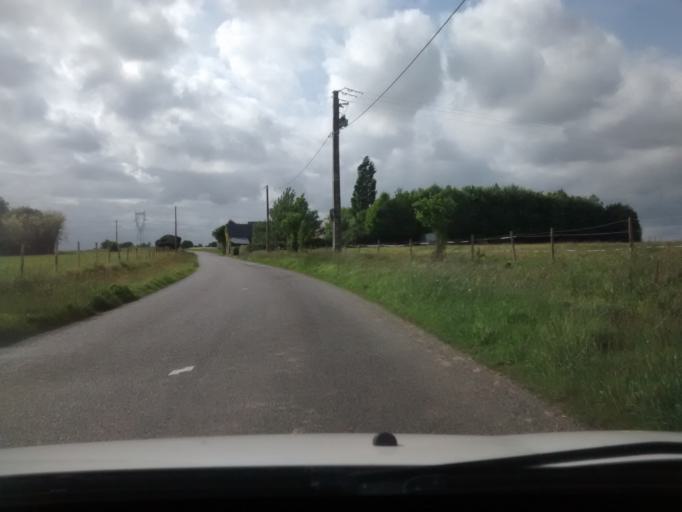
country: FR
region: Brittany
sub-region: Departement d'Ille-et-Vilaine
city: Nouvoitou
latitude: 48.0682
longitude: -1.5299
